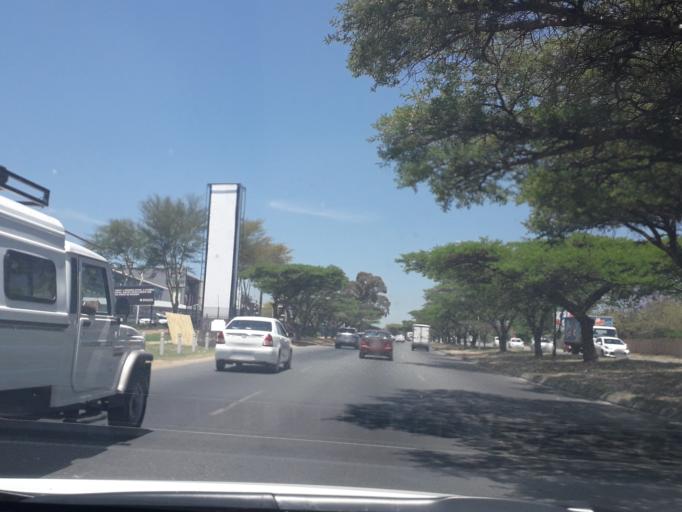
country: ZA
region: Gauteng
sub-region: City of Johannesburg Metropolitan Municipality
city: Diepsloot
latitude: -26.0289
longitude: 28.0097
